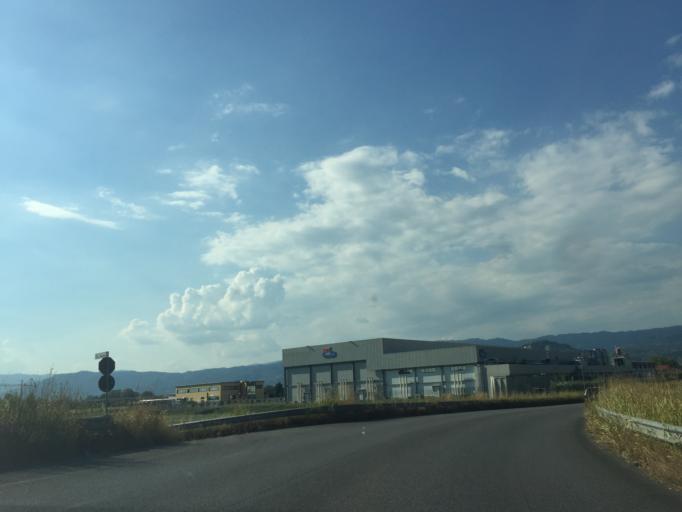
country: IT
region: Tuscany
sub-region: Provincia di Pistoia
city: Monsummano Terme
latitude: 43.8561
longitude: 10.8029
